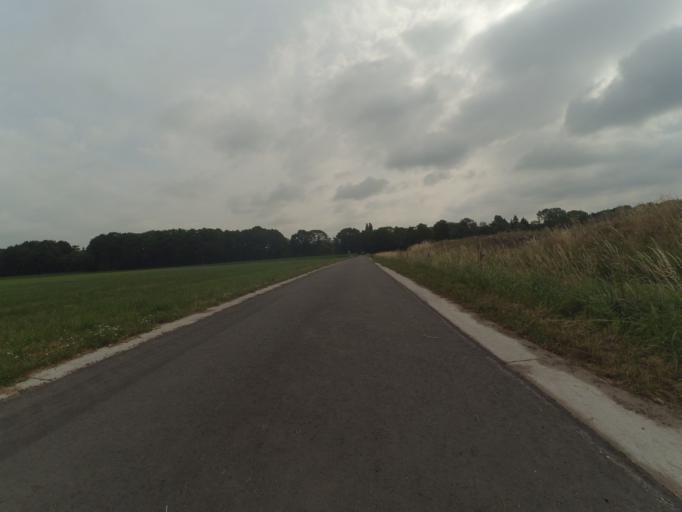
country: BE
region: Flanders
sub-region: Provincie Antwerpen
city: Essen
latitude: 51.4620
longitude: 4.4224
